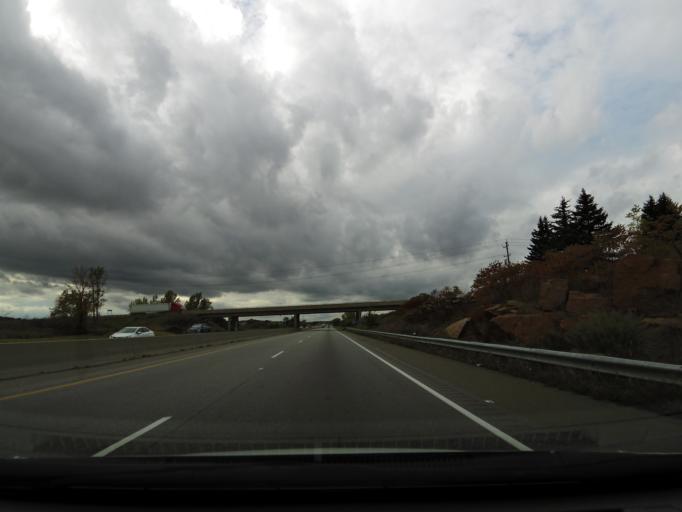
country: CA
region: Ontario
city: Gananoque
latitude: 44.3232
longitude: -76.3297
